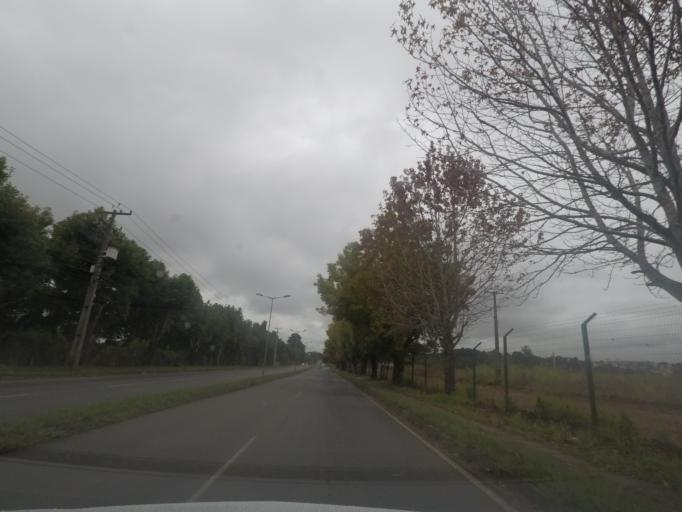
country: BR
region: Parana
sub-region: Pinhais
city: Pinhais
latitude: -25.3930
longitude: -49.1716
